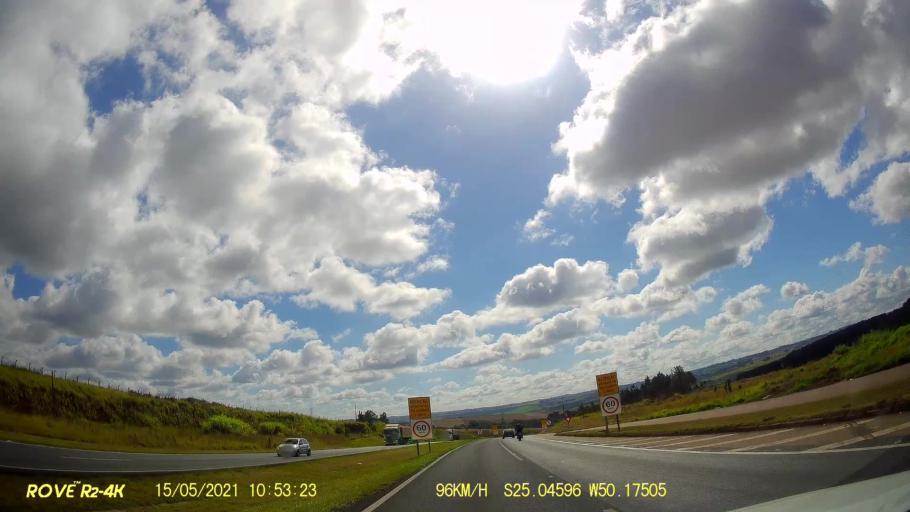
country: BR
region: Parana
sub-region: Ponta Grossa
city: Ponta Grossa
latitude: -25.0458
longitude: -50.1768
